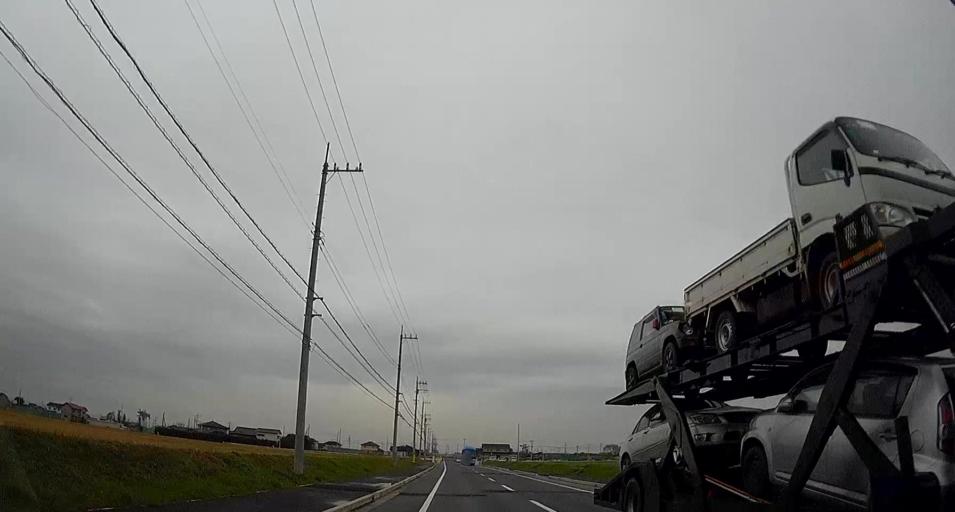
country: JP
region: Chiba
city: Kisarazu
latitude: 35.4271
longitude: 139.9144
